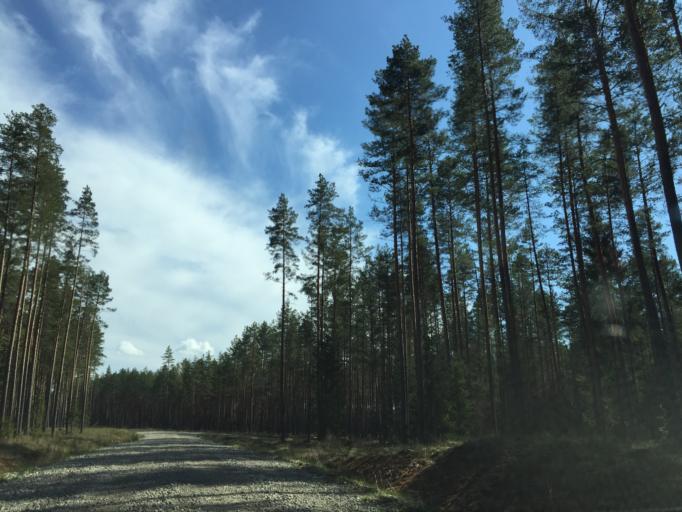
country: LV
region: Strenci
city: Strenci
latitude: 57.5854
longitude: 25.7063
